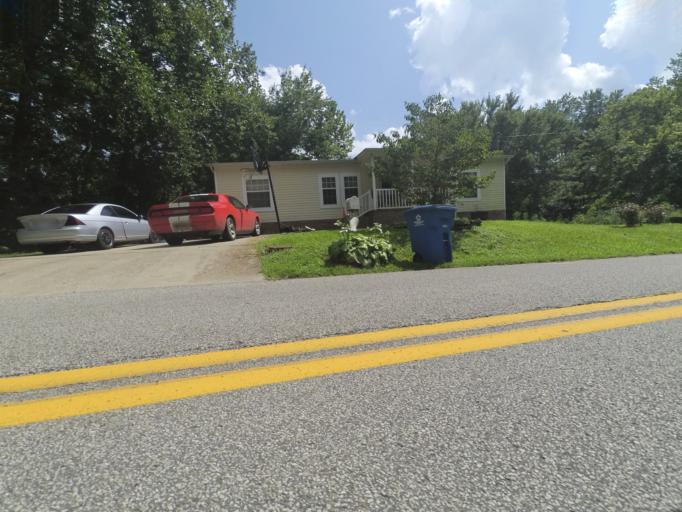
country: US
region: West Virginia
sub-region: Cabell County
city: Pea Ridge
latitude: 38.4282
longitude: -82.3139
